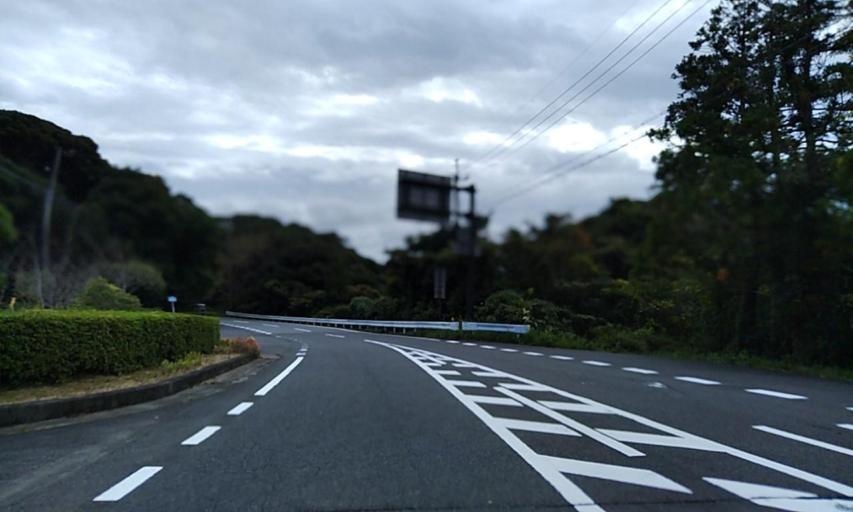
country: JP
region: Wakayama
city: Shingu
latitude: 33.4719
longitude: 135.8175
